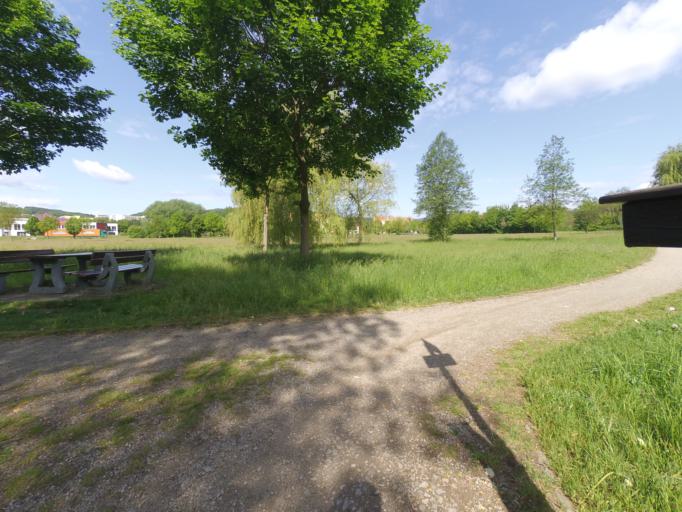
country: DE
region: Thuringia
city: Rudolstadt
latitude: 50.7007
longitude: 11.3331
